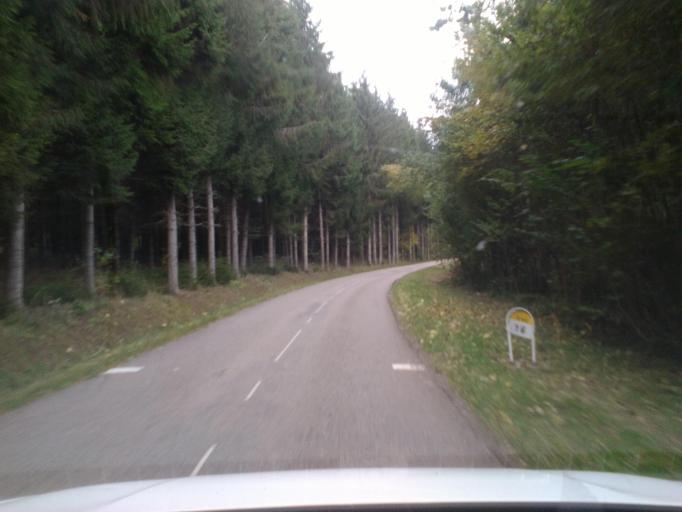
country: FR
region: Lorraine
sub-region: Departement des Vosges
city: Sainte-Marguerite
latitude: 48.3257
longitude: 7.0230
